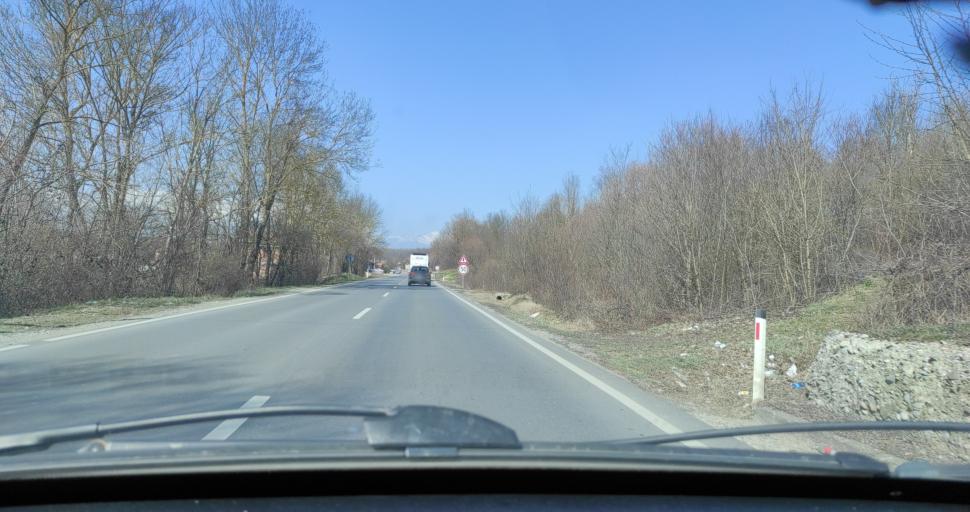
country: XK
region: Pec
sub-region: Komuna e Pejes
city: Kosuriq
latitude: 42.6325
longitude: 20.4497
